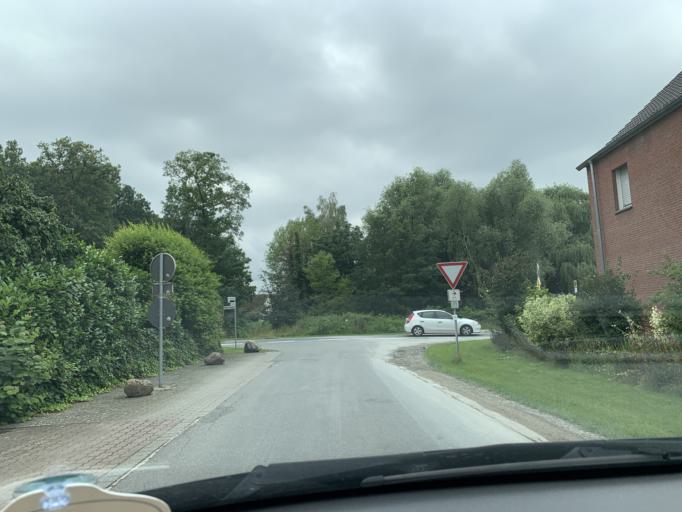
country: DE
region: North Rhine-Westphalia
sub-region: Regierungsbezirk Munster
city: Ennigerloh
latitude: 51.8311
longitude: 8.0714
